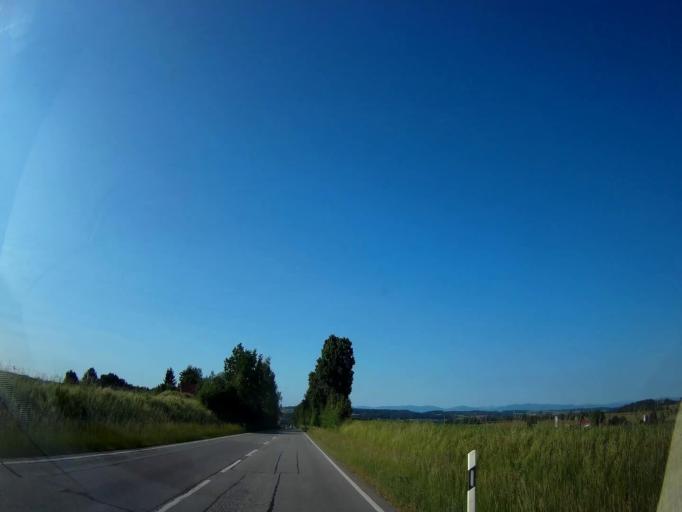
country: DE
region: Bavaria
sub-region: Lower Bavaria
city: Simbach
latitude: 48.5928
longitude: 12.7187
